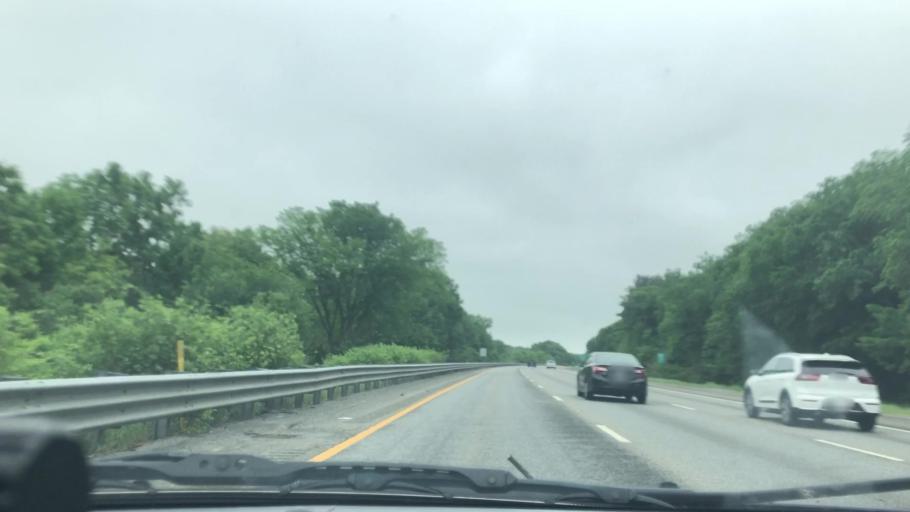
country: US
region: Massachusetts
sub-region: Worcester County
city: Bolton
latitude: 42.4413
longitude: -71.5881
